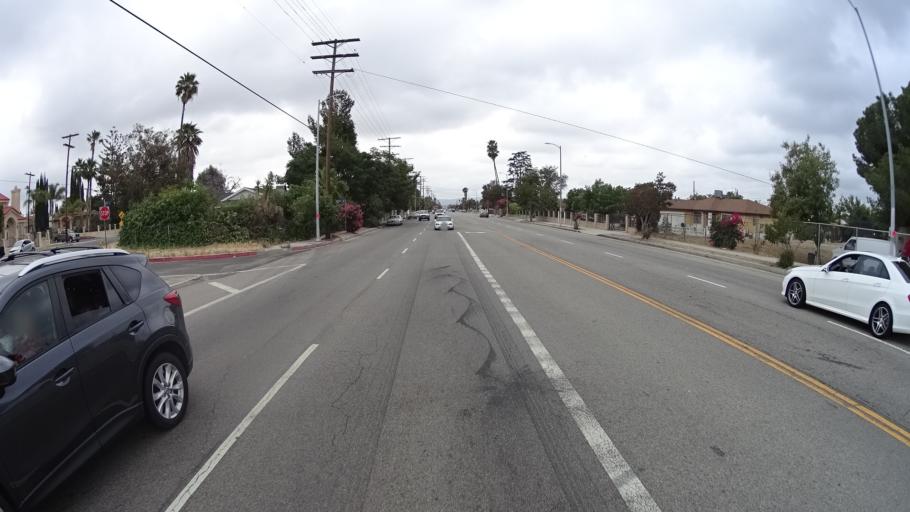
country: US
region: California
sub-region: Los Angeles County
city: Van Nuys
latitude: 34.2176
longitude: -118.4144
